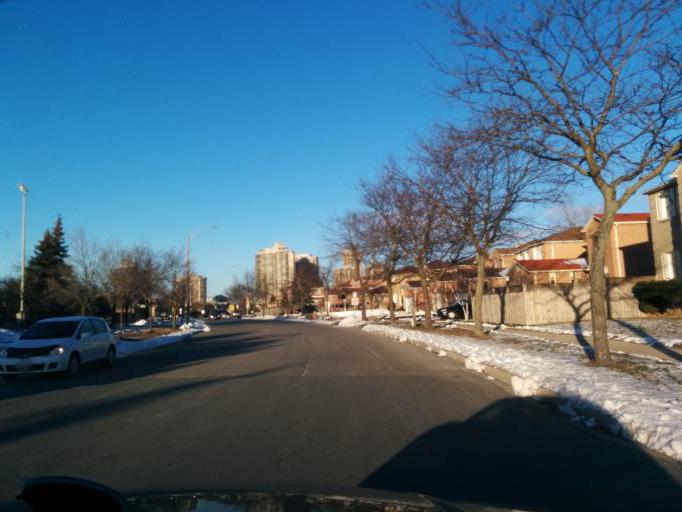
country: CA
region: Ontario
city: Mississauga
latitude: 43.5963
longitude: -79.6566
